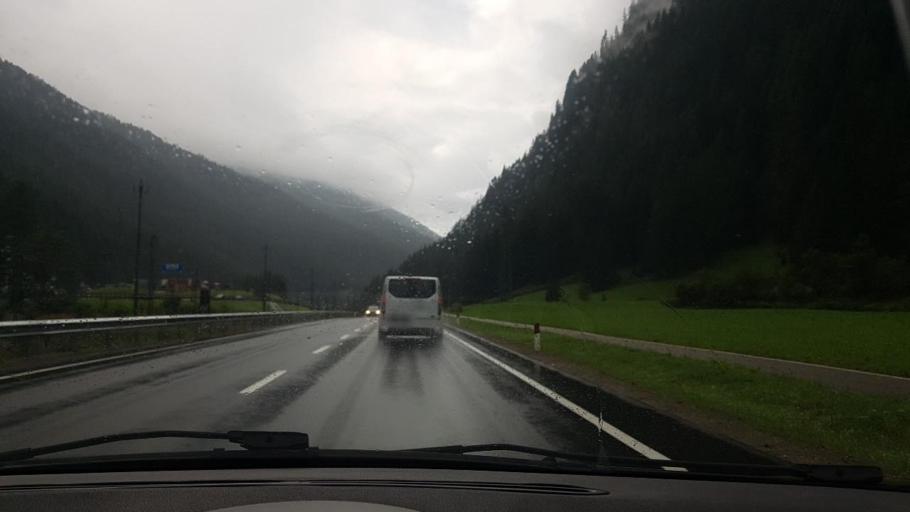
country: AT
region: Tyrol
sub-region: Politischer Bezirk Innsbruck Land
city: Gries am Brenner
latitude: 46.9926
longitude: 11.4980
